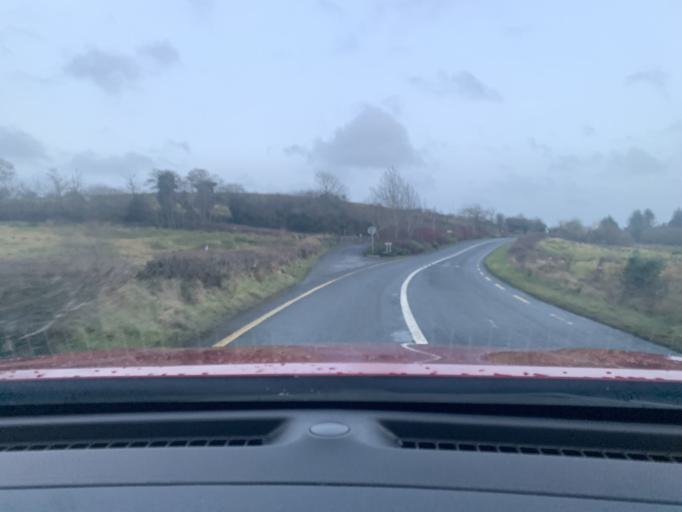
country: IE
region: Connaught
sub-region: Sligo
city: Ballymote
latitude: 54.0385
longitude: -8.4304
